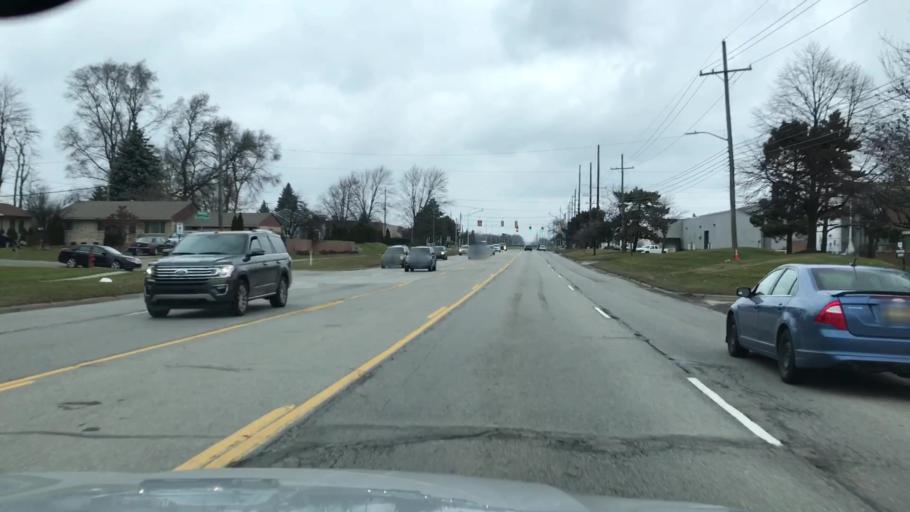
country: US
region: Michigan
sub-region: Wayne County
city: Westland
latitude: 42.3728
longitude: -83.4115
